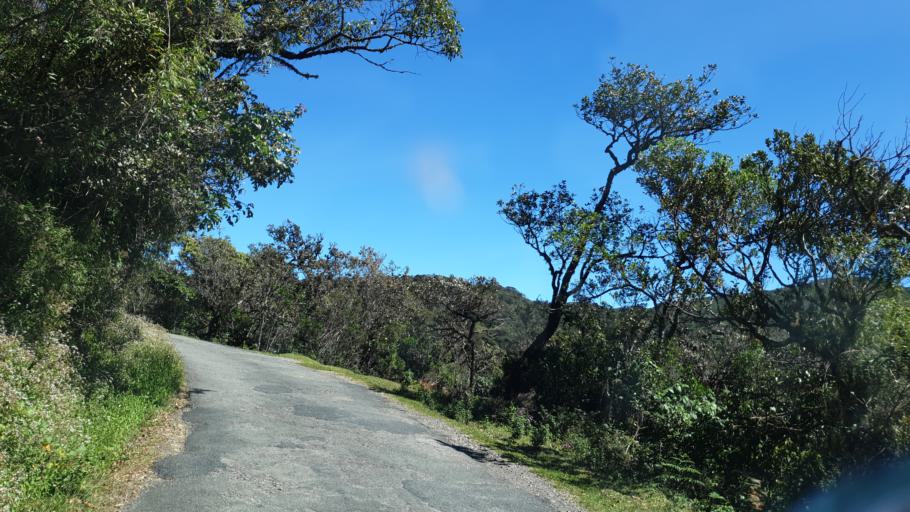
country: LK
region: Central
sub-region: Nuwara Eliya District
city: Nuwara Eliya
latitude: 6.8339
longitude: 80.8098
